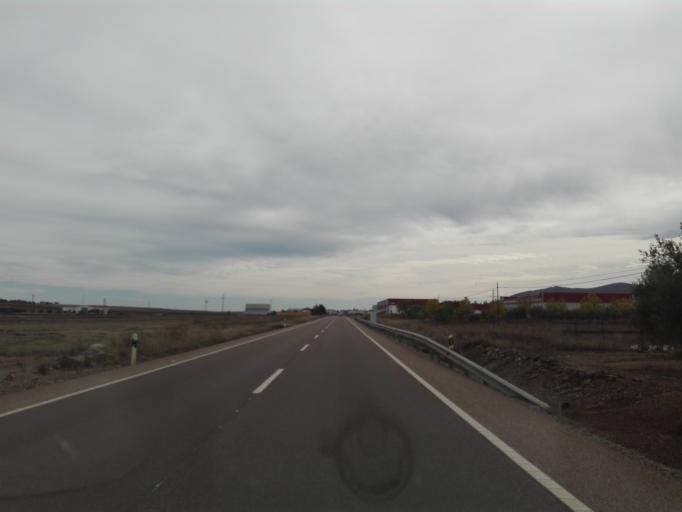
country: ES
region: Extremadura
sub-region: Provincia de Badajoz
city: Llerena
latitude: 38.2568
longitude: -6.0341
